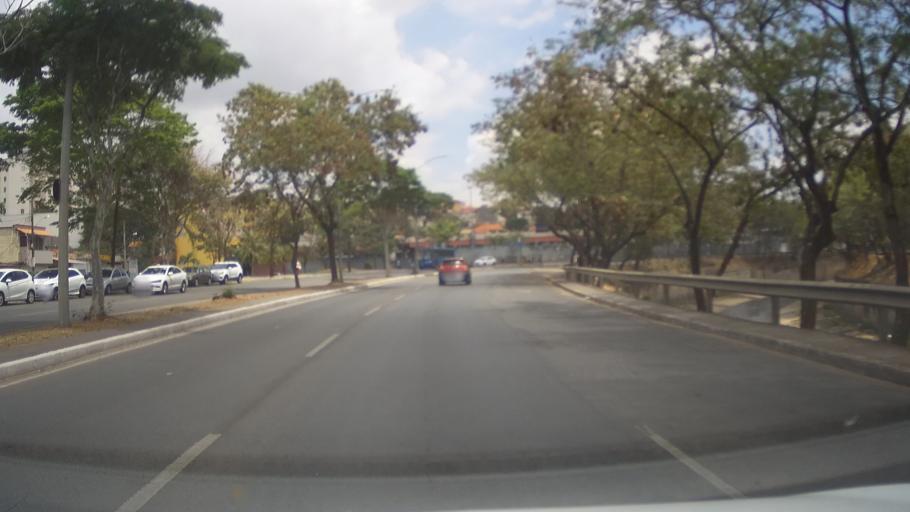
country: BR
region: Minas Gerais
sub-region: Belo Horizonte
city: Belo Horizonte
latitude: -19.9052
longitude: -43.8972
